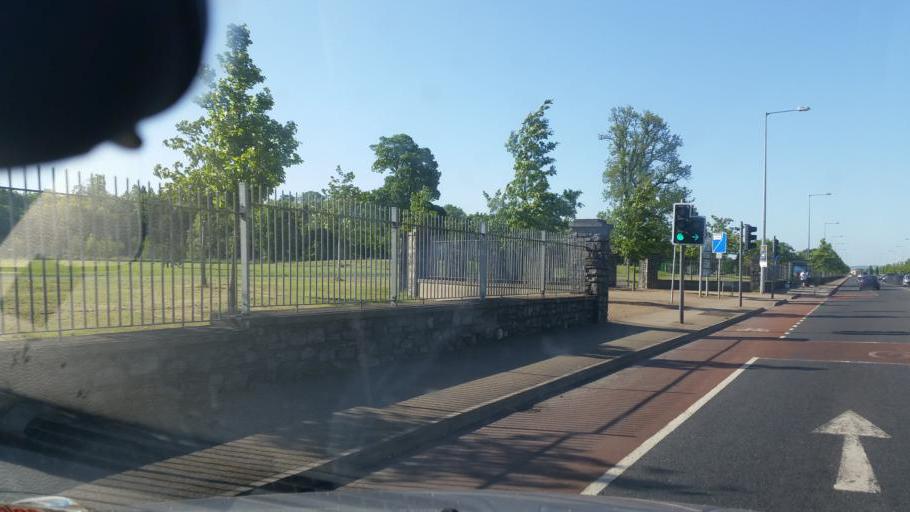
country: IE
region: Leinster
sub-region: Fingal County
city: Blanchardstown
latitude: 53.3905
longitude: -6.4002
